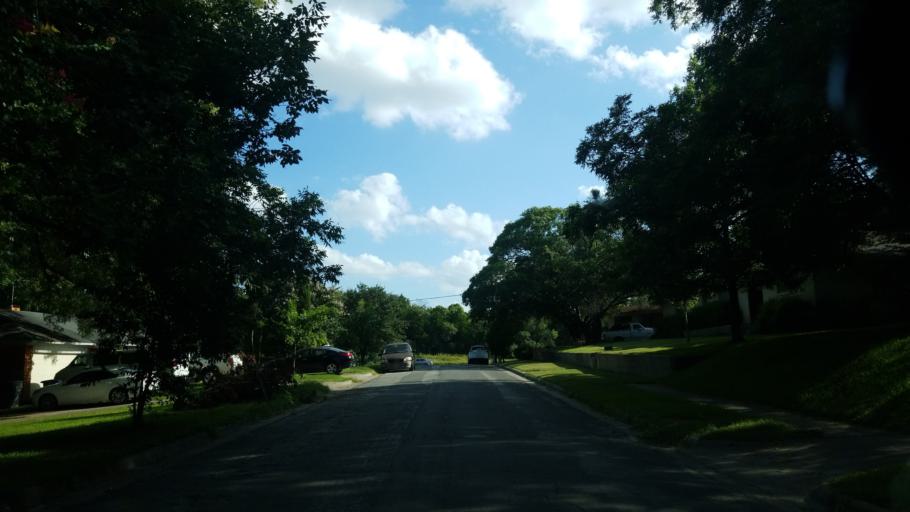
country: US
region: Texas
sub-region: Dallas County
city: Balch Springs
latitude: 32.7642
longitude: -96.7065
